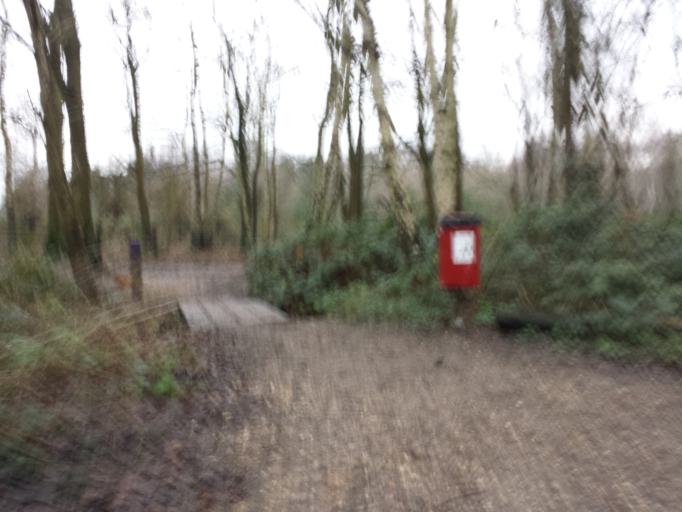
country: GB
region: England
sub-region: Surrey
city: Bagshot
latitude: 51.3515
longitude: -0.6842
